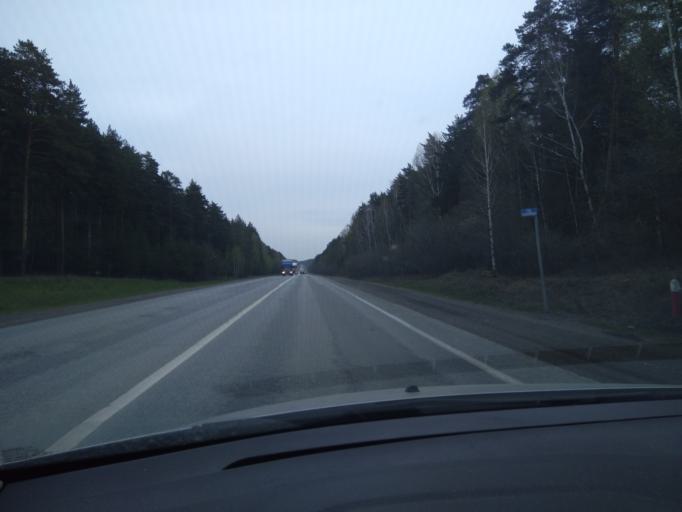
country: RU
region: Sverdlovsk
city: Gryaznovskoye
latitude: 56.7887
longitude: 61.7330
